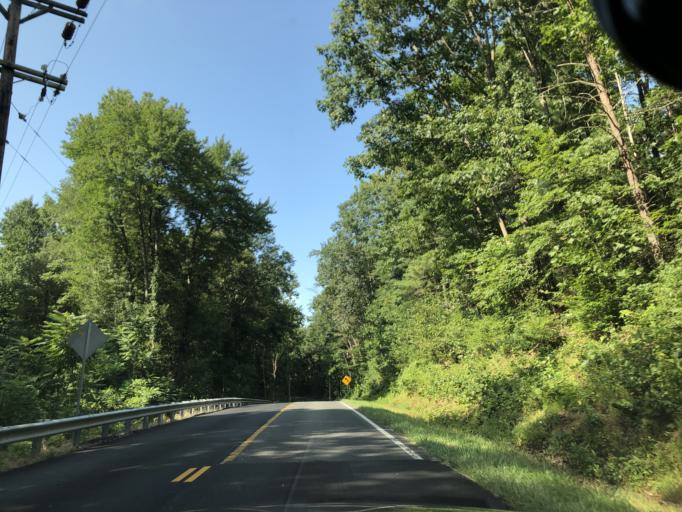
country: US
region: Maryland
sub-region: Frederick County
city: Linganore
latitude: 39.4304
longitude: -77.1799
